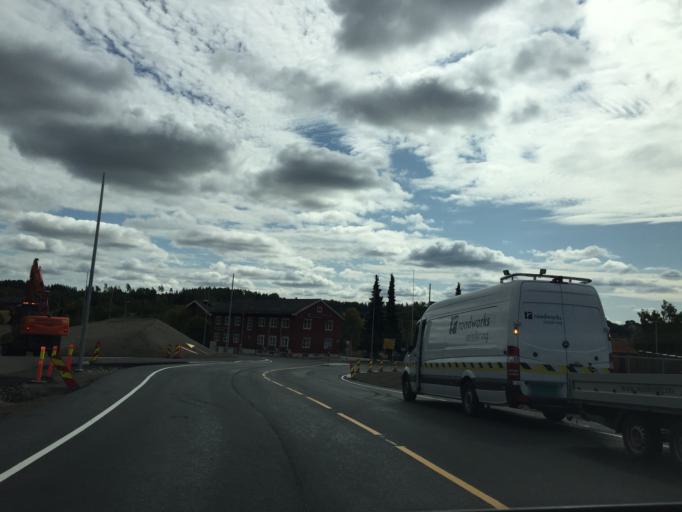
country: NO
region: Ostfold
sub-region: Hobol
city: Elvestad
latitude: 59.6233
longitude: 10.9483
